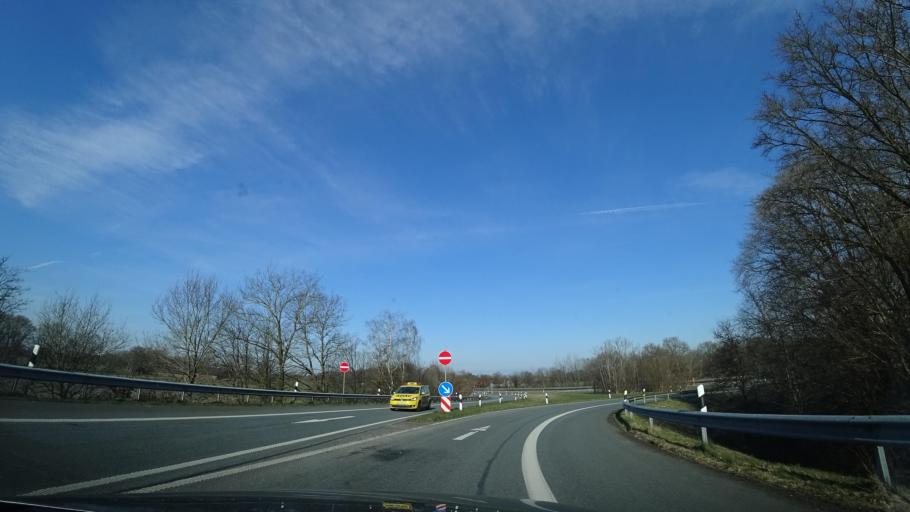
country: DE
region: Lower Saxony
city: Hatten
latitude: 53.0621
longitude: 8.3520
